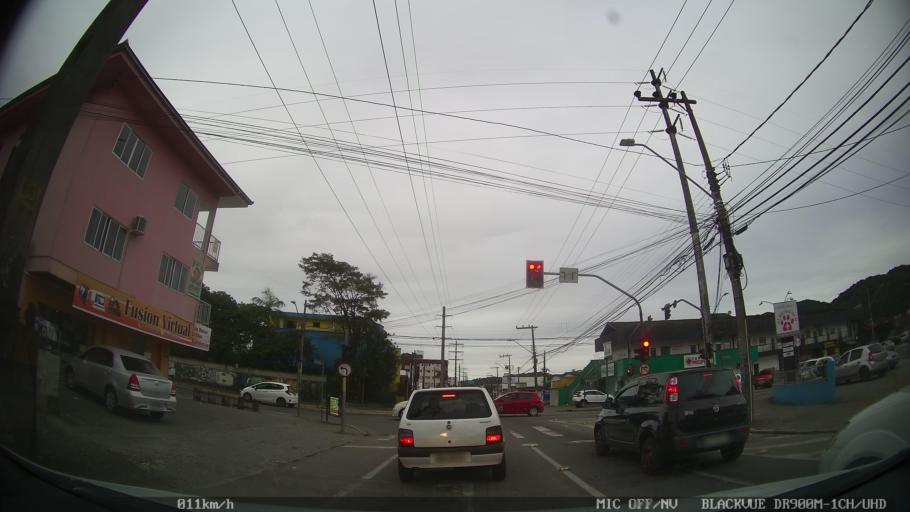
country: BR
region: Santa Catarina
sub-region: Joinville
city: Joinville
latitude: -26.2728
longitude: -48.8259
